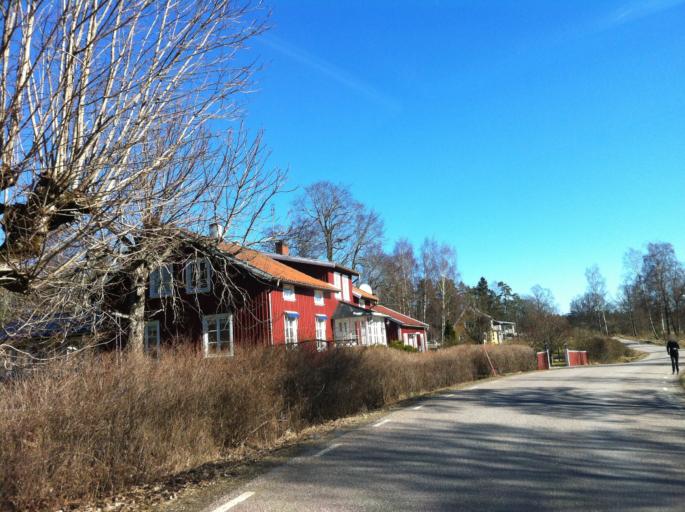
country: SE
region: Vaestra Goetaland
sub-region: Grastorps Kommun
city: Graestorp
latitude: 58.3990
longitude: 12.5702
